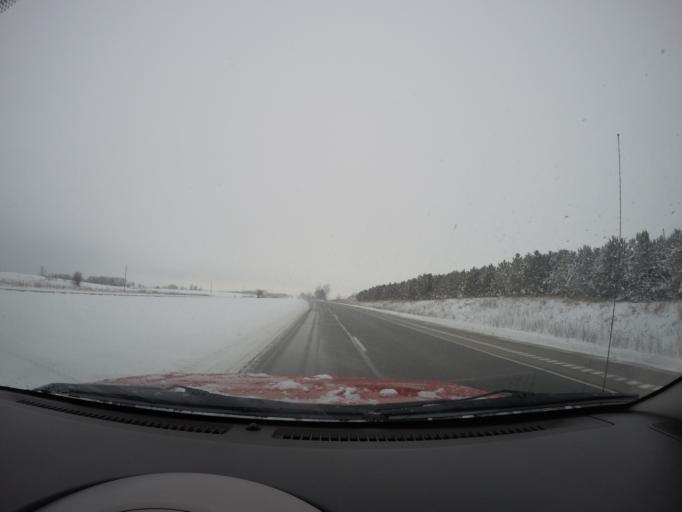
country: US
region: Minnesota
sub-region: Winona County
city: Lewiston
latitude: 43.9380
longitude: -91.7866
